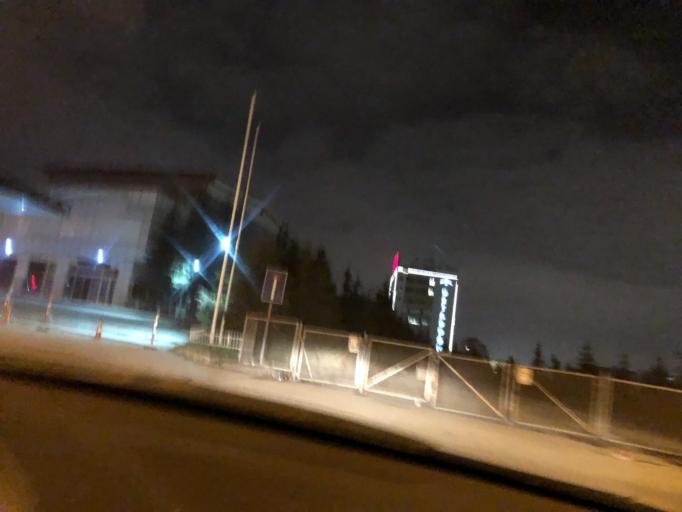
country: TR
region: Ankara
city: Batikent
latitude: 39.9641
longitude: 32.7977
